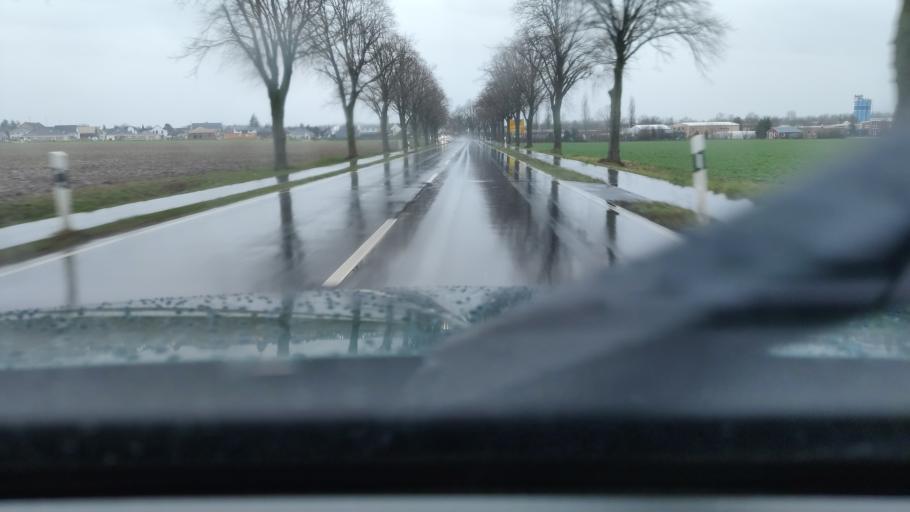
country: DE
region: Lower Saxony
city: Ilsede
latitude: 52.2773
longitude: 10.2263
